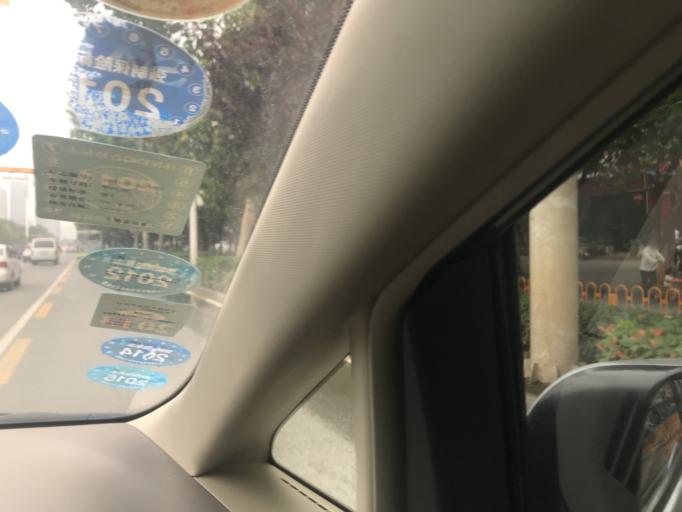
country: CN
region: Hubei
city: Jiang'an
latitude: 30.6081
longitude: 114.3437
